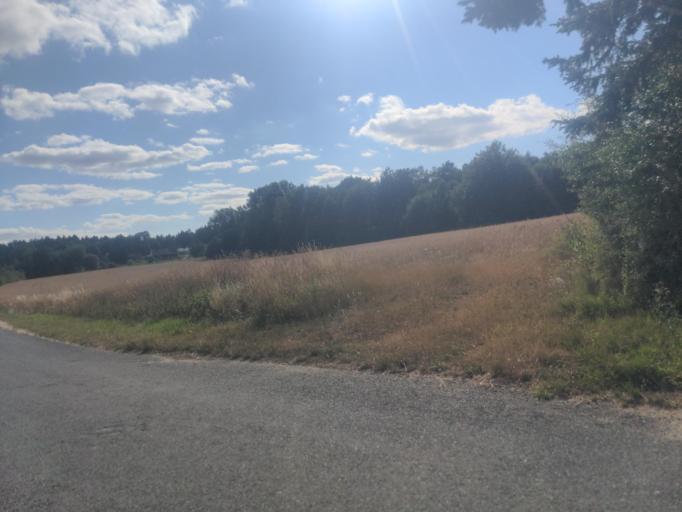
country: DE
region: Lower Saxony
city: Neu Darchau
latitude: 53.2067
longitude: 10.8572
